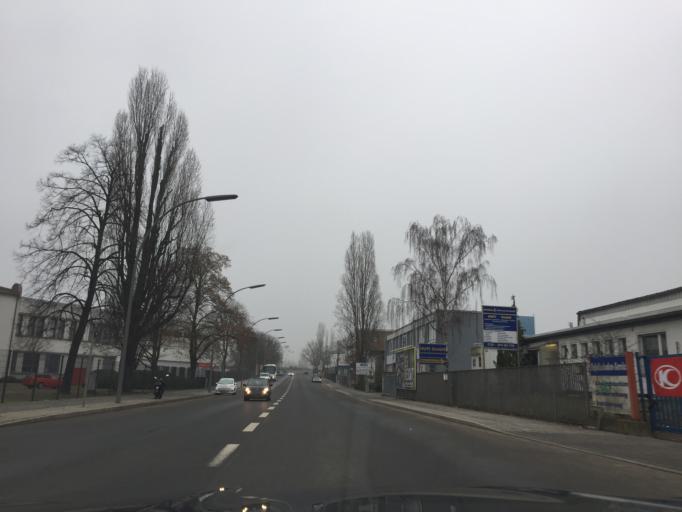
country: DE
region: Berlin
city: Haselhorst
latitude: 52.5281
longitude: 13.2415
